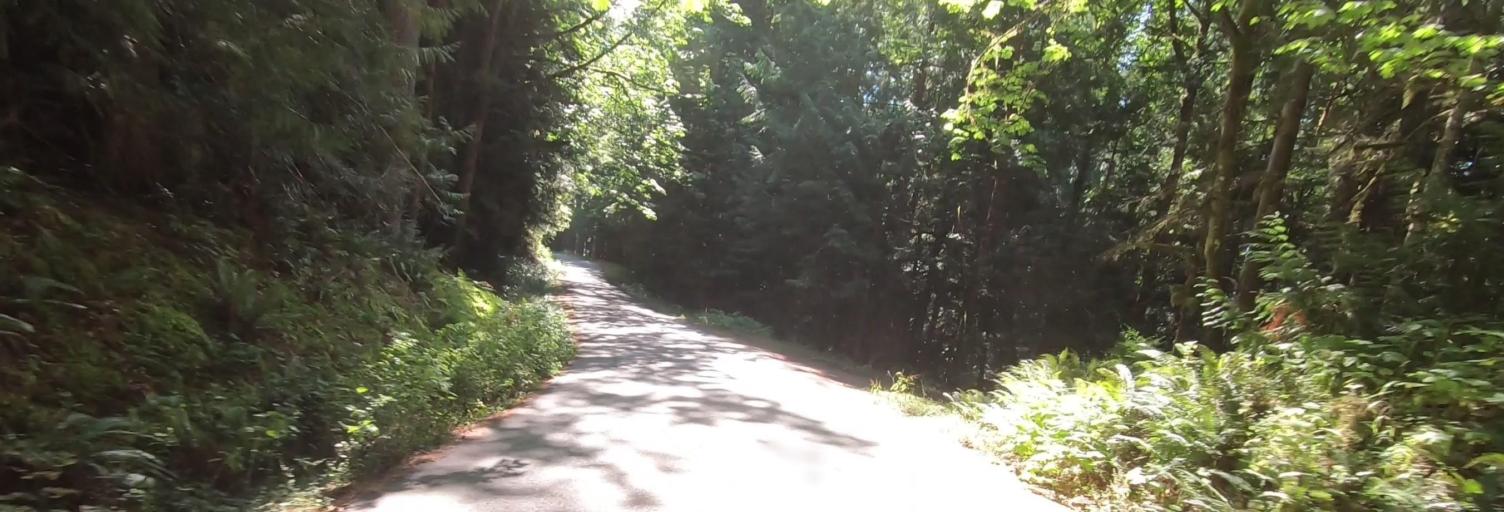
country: US
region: Washington
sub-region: Whatcom County
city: Peaceful Valley
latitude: 48.9034
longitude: -121.9300
